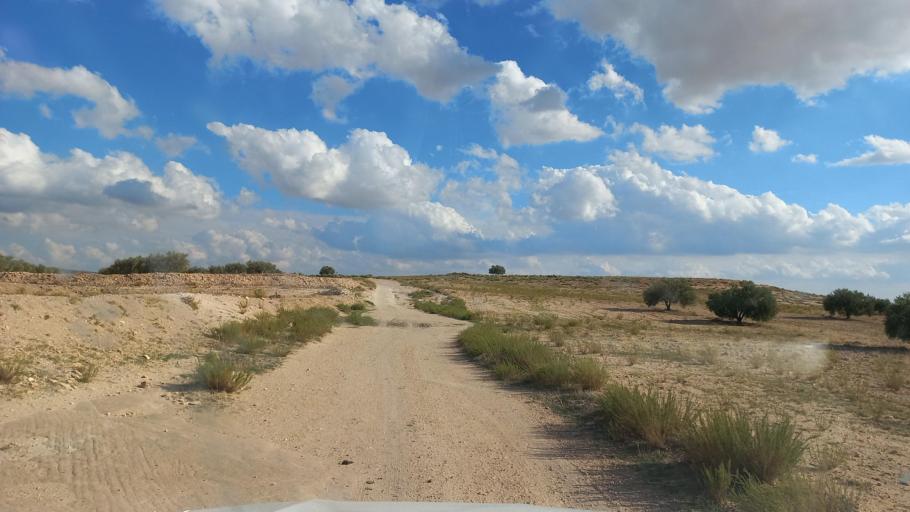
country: TN
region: Al Qasrayn
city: Sbiba
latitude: 35.3955
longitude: 9.0398
